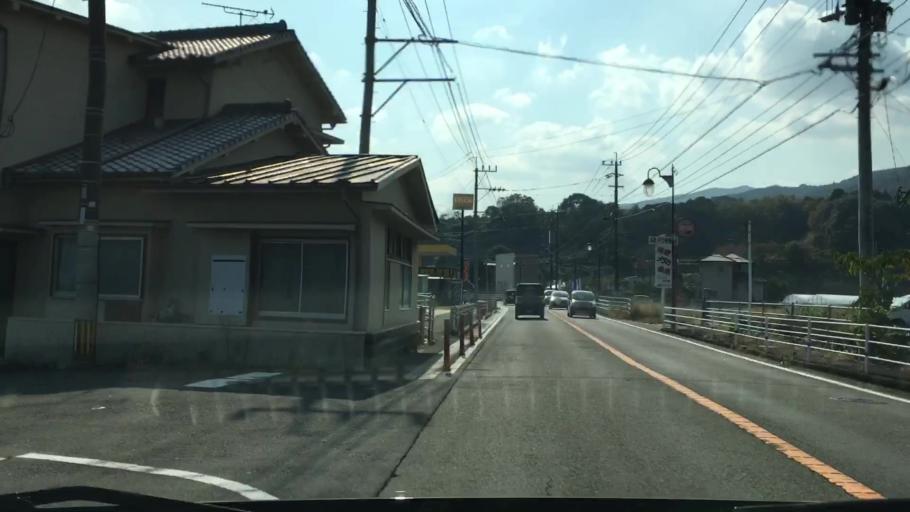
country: JP
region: Nagasaki
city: Togitsu
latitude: 32.9460
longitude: 129.7828
